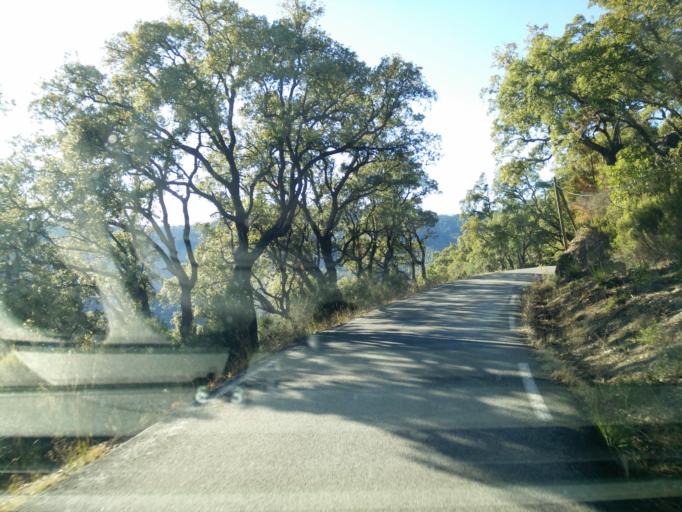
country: FR
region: Provence-Alpes-Cote d'Azur
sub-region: Departement du Var
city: La Garde-Freinet
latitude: 43.2589
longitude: 6.4484
